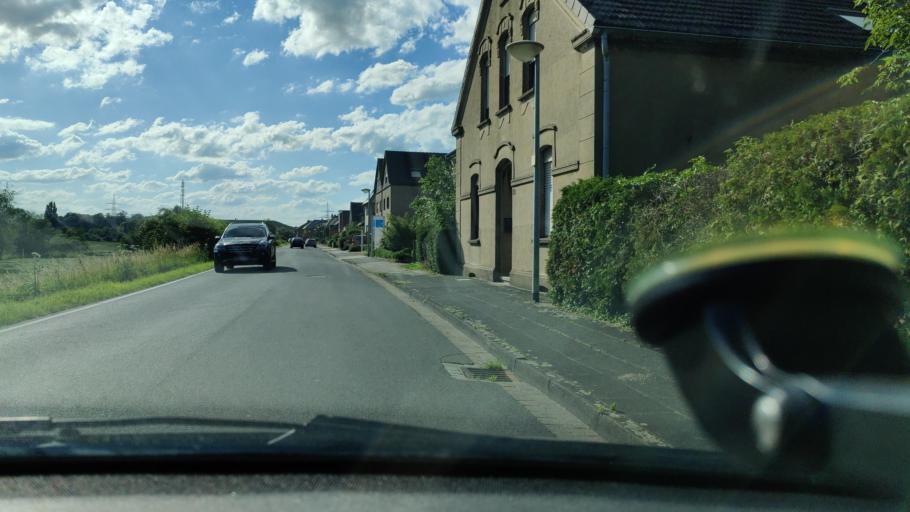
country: DE
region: North Rhine-Westphalia
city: Rheinberg
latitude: 51.5516
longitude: 6.5884
